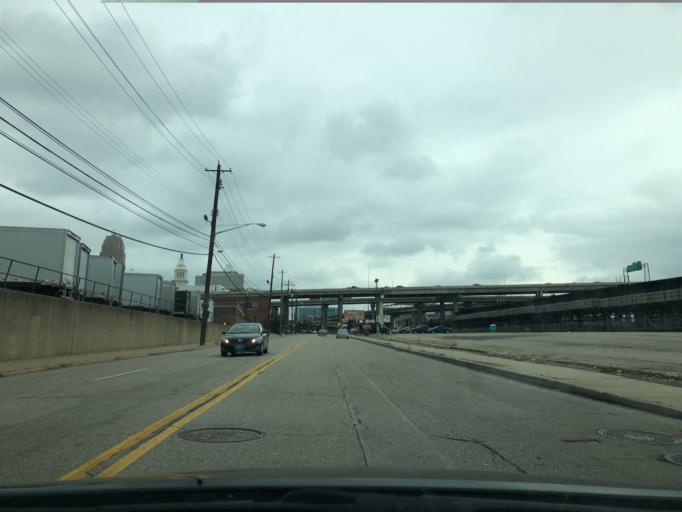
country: US
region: Kentucky
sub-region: Kenton County
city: Covington
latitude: 39.0972
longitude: -84.5250
